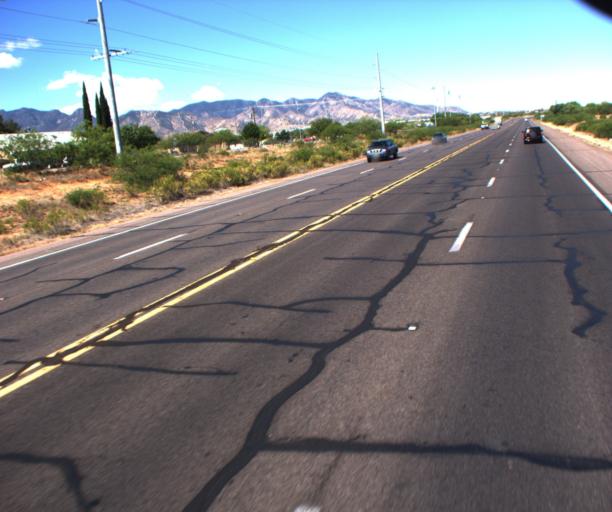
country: US
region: Arizona
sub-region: Cochise County
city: Sierra Vista
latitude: 31.5695
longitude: -110.2982
